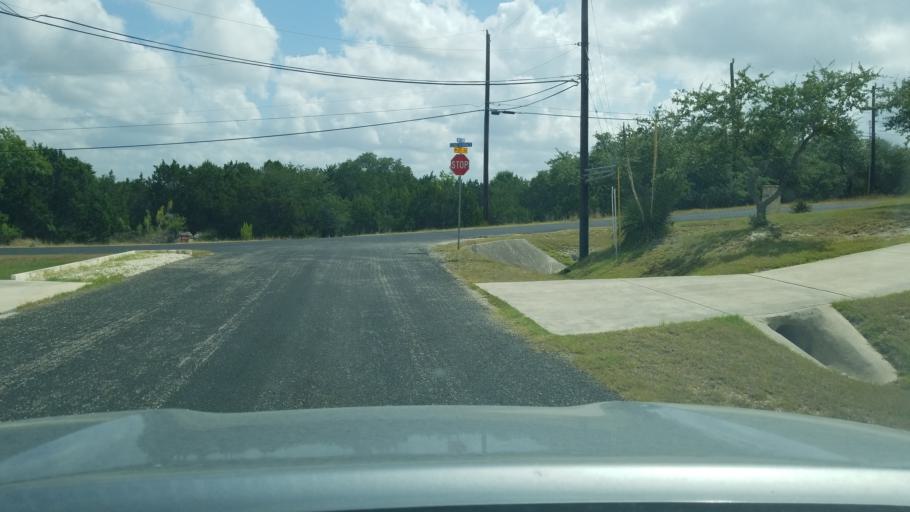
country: US
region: Texas
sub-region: Bexar County
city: Timberwood Park
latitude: 29.6842
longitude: -98.5131
